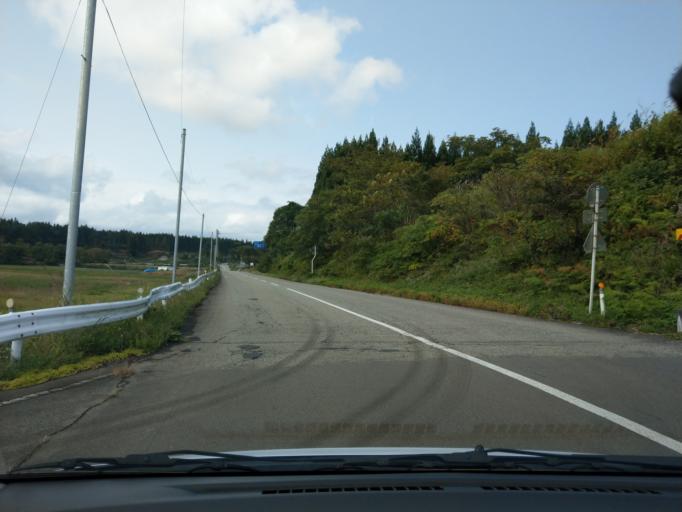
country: JP
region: Akita
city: Omagari
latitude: 39.5190
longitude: 140.3046
